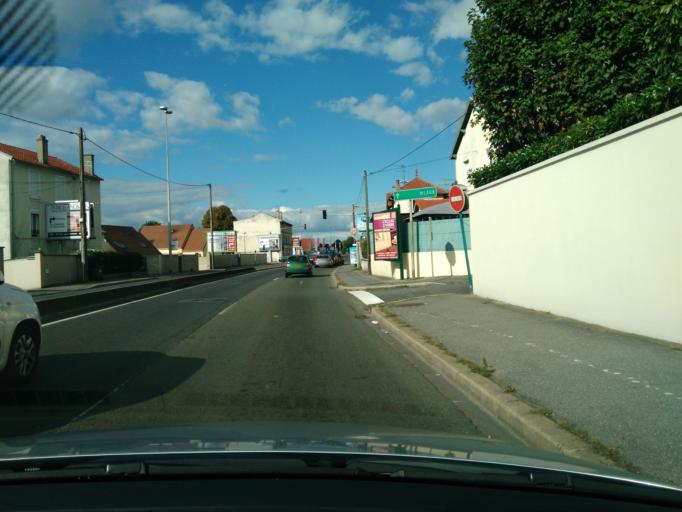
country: FR
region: Ile-de-France
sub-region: Departement de Seine-et-Marne
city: Meaux
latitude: 48.9452
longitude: 2.8795
